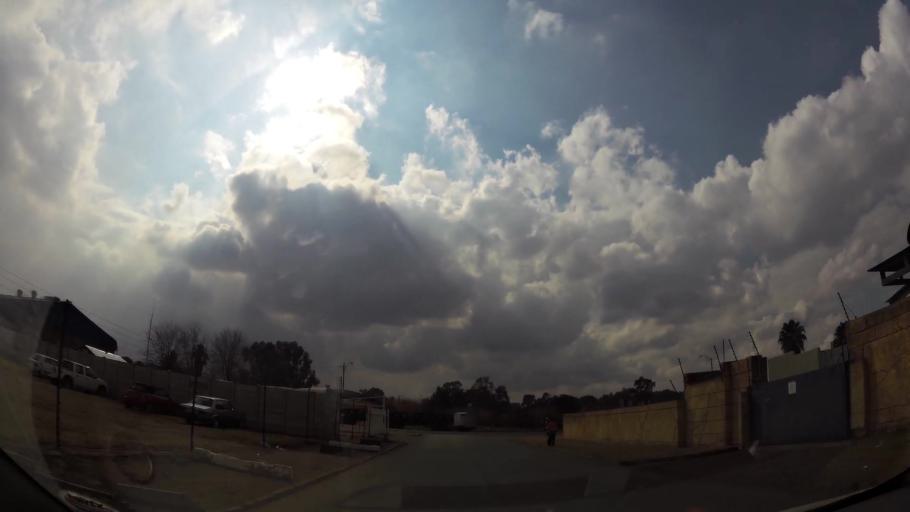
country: ZA
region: Gauteng
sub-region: Sedibeng District Municipality
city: Vereeniging
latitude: -26.6597
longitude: 27.9268
